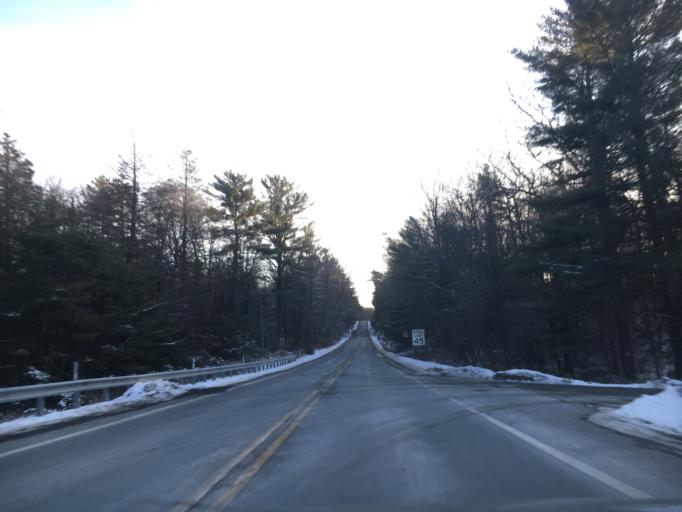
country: US
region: Pennsylvania
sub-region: Pike County
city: Hemlock Farms
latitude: 41.3646
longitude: -75.1279
